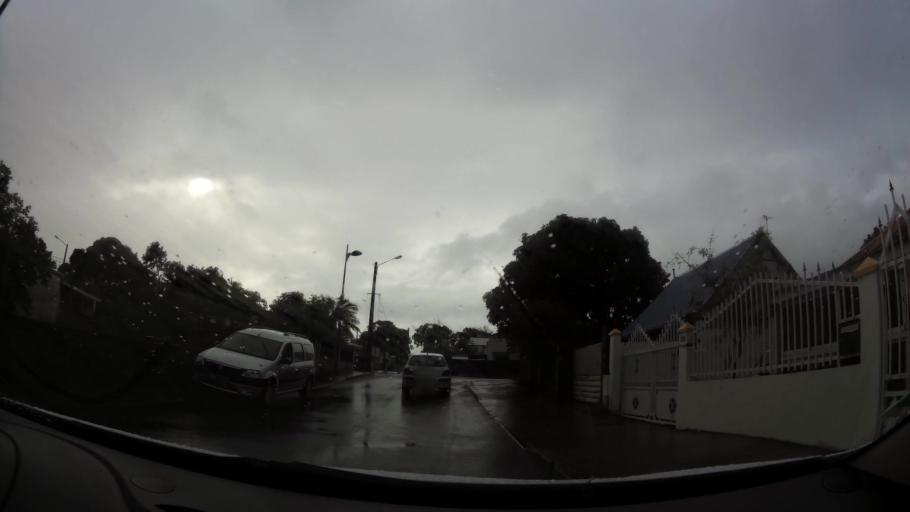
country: RE
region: Reunion
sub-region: Reunion
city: Saint-Andre
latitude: -20.9776
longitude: 55.6598
